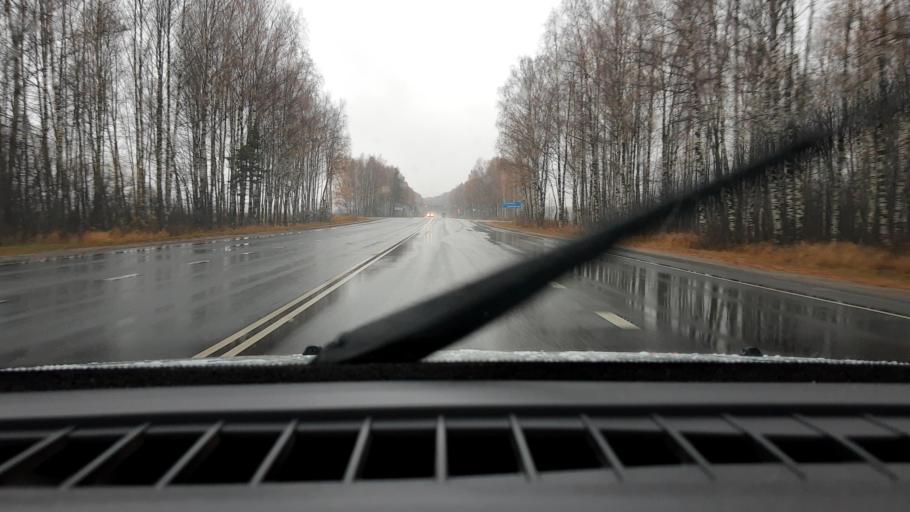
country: RU
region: Nizjnij Novgorod
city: Linda
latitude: 56.6570
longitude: 44.1227
